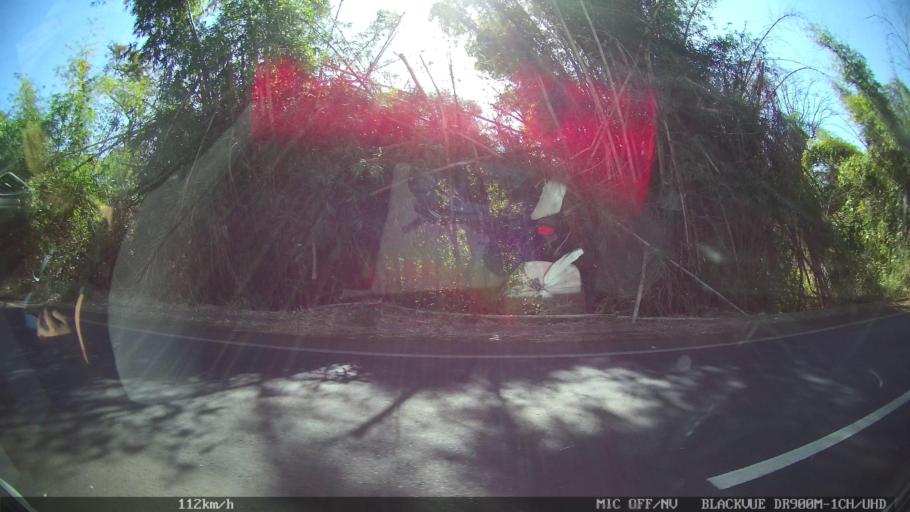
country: BR
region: Sao Paulo
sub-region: Barretos
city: Barretos
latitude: -20.5972
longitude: -48.7201
